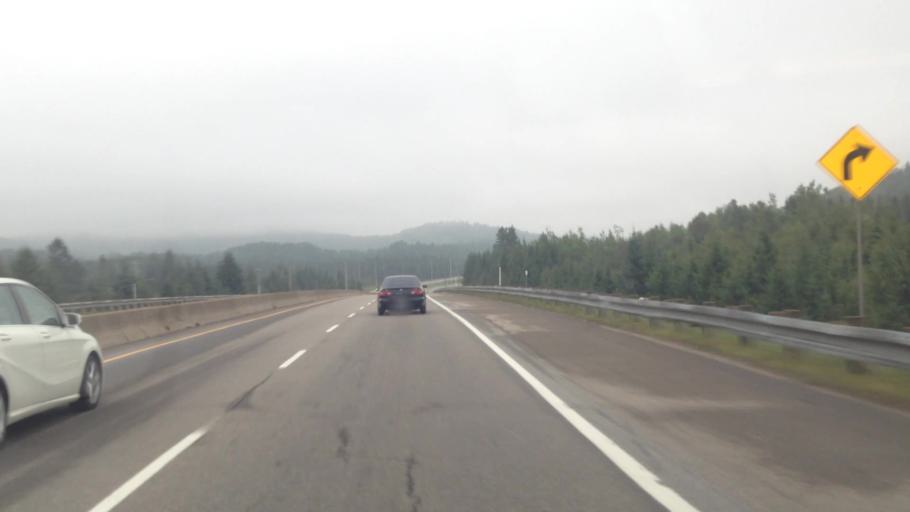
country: CA
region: Quebec
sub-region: Laurentides
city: Sainte-Agathe-des-Monts
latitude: 46.0980
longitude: -74.3625
